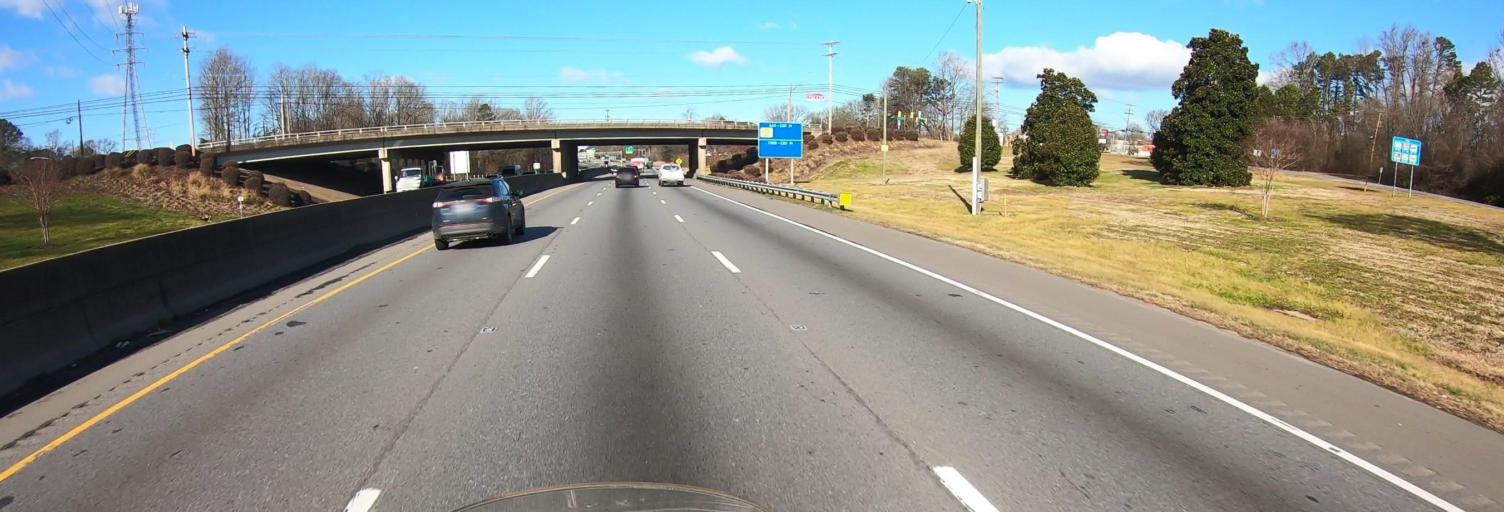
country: US
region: North Carolina
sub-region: Gaston County
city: Ranlo
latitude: 35.2682
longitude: -81.1493
